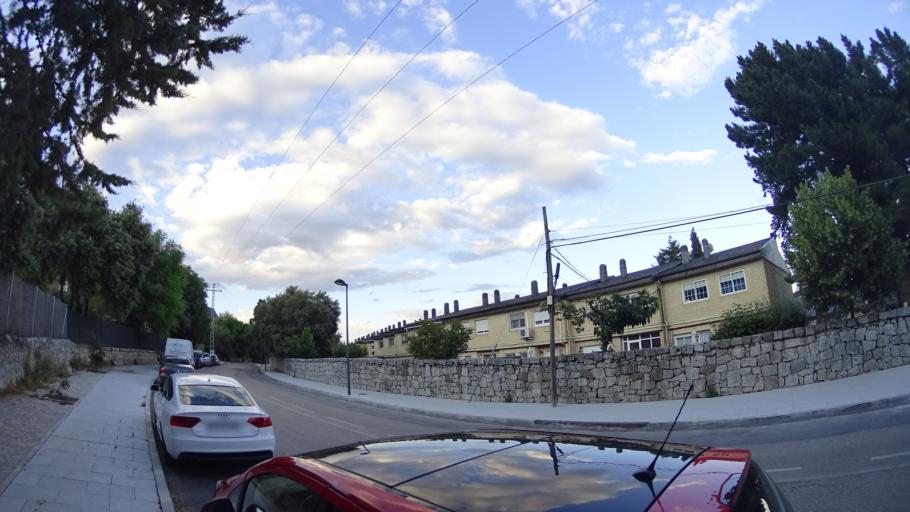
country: ES
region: Madrid
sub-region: Provincia de Madrid
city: Hoyo de Manzanares
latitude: 40.6294
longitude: -3.8996
